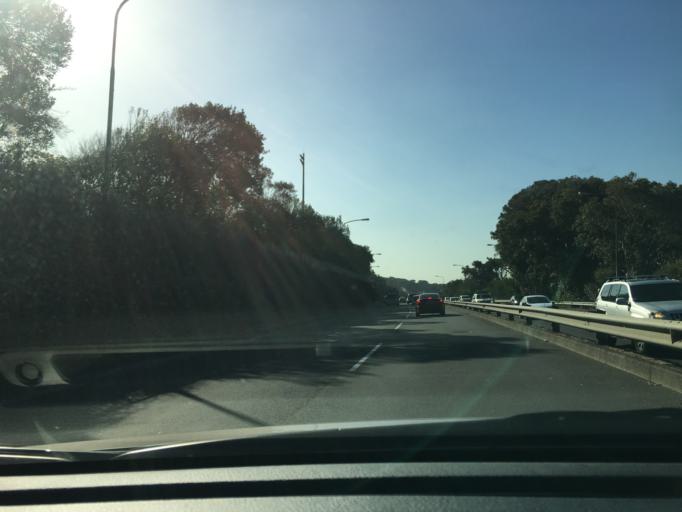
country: ZA
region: Western Cape
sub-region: City of Cape Town
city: Rosebank
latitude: -33.9580
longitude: 18.4637
